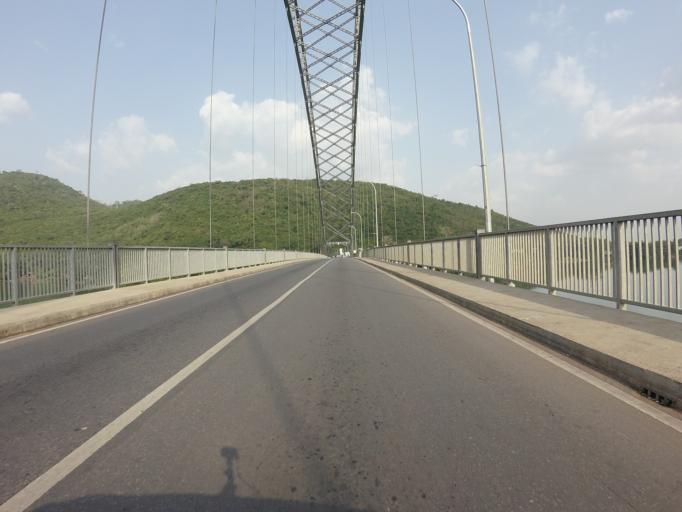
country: GH
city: Akropong
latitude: 6.2397
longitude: 0.0950
